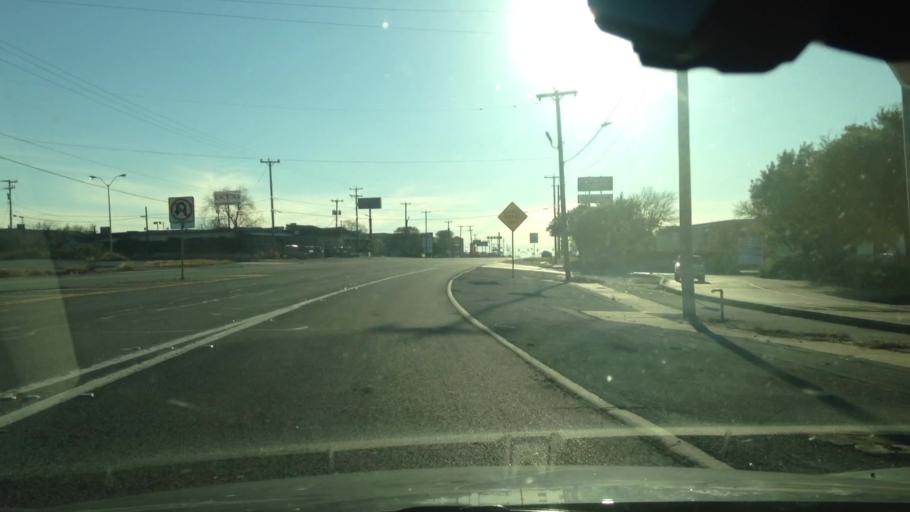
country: US
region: Texas
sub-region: Bexar County
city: Windcrest
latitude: 29.5128
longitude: -98.4047
